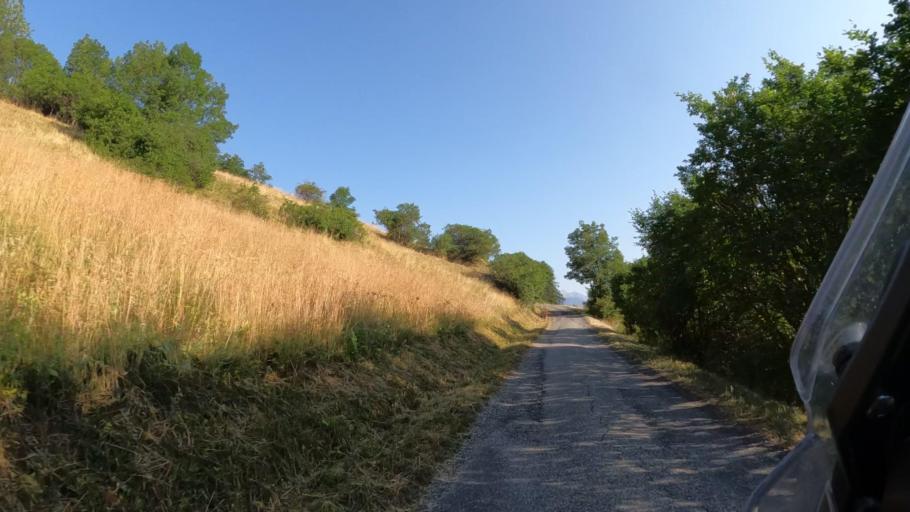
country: FR
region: Provence-Alpes-Cote d'Azur
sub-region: Departement des Hautes-Alpes
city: Guillestre
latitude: 44.6060
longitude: 6.6840
